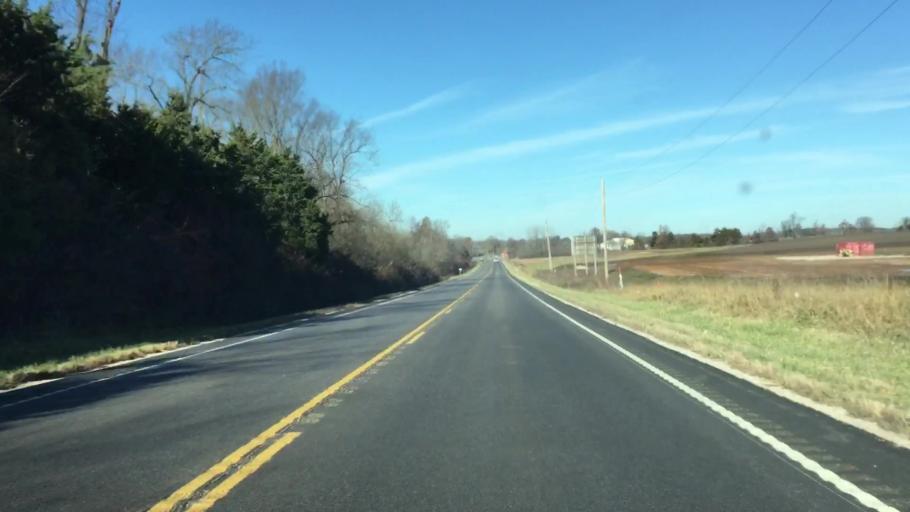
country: US
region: Missouri
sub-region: Miller County
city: Eldon
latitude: 38.3575
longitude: -92.6012
